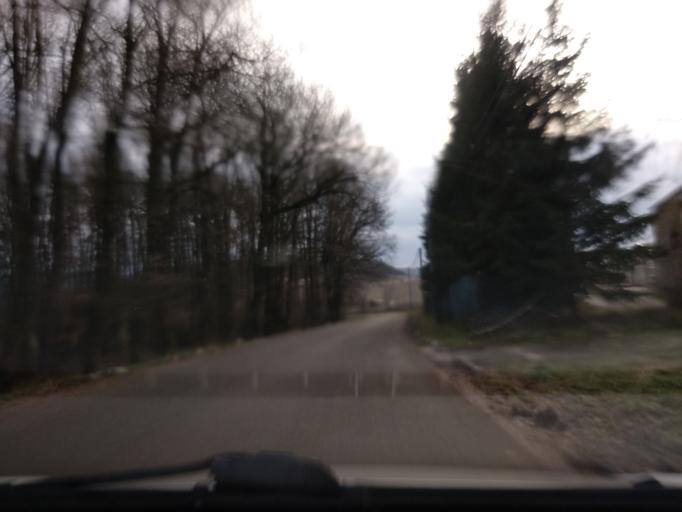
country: CZ
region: South Moravian
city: Lipuvka
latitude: 49.3778
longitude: 16.5590
